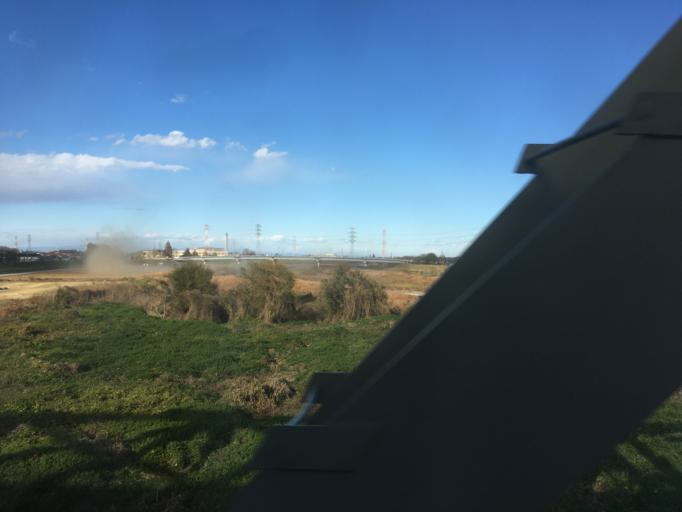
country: JP
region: Saitama
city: Kawagoe
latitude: 35.9235
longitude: 139.4527
